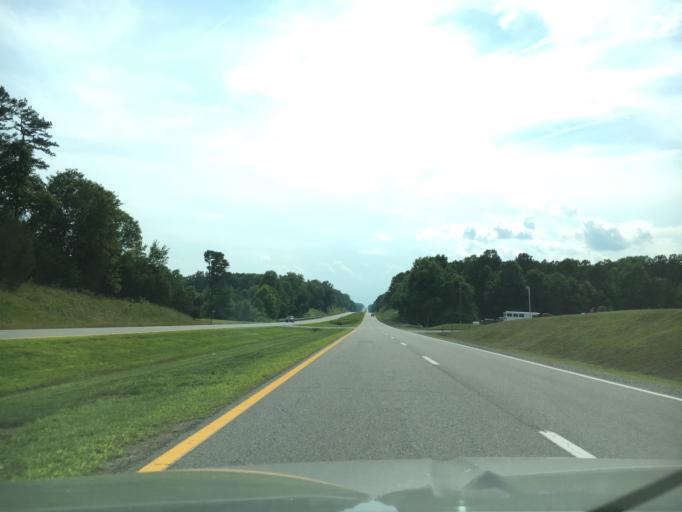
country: US
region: Virginia
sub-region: Mecklenburg County
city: Chase City
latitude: 36.8322
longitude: -78.6676
